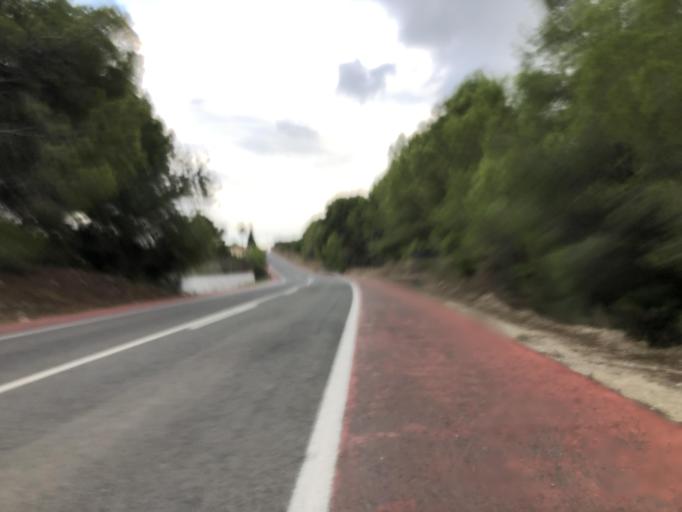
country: ES
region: Valencia
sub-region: Provincia de Alicante
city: Polop
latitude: 38.6334
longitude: -0.1516
